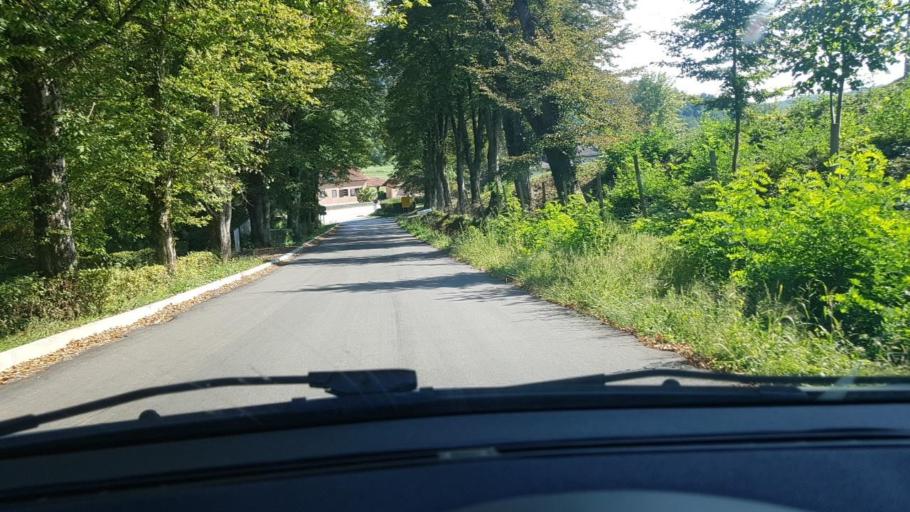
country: HR
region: Karlovacka
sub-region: Grad Karlovac
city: Karlovac
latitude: 45.4782
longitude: 15.4478
